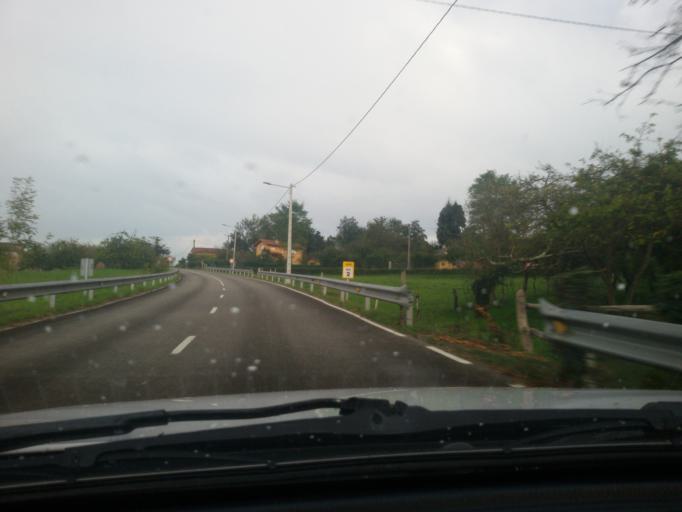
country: ES
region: Asturias
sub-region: Province of Asturias
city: Norena
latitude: 43.3682
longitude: -5.7492
